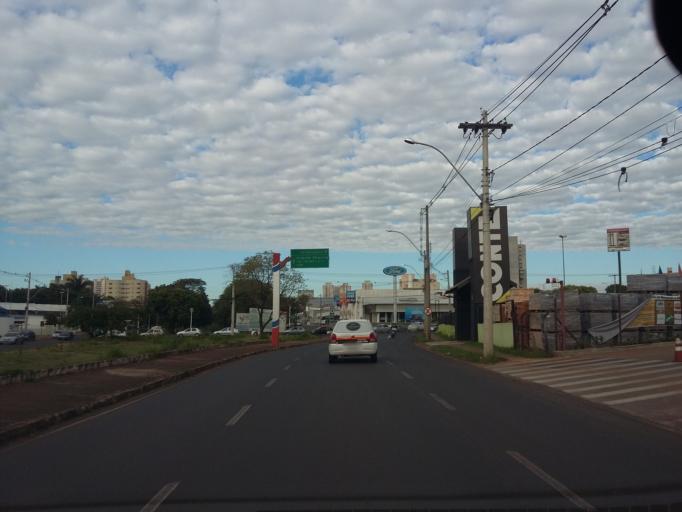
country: BR
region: Sao Paulo
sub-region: Sao Jose Do Rio Preto
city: Sao Jose do Rio Preto
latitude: -20.8258
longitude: -49.4038
